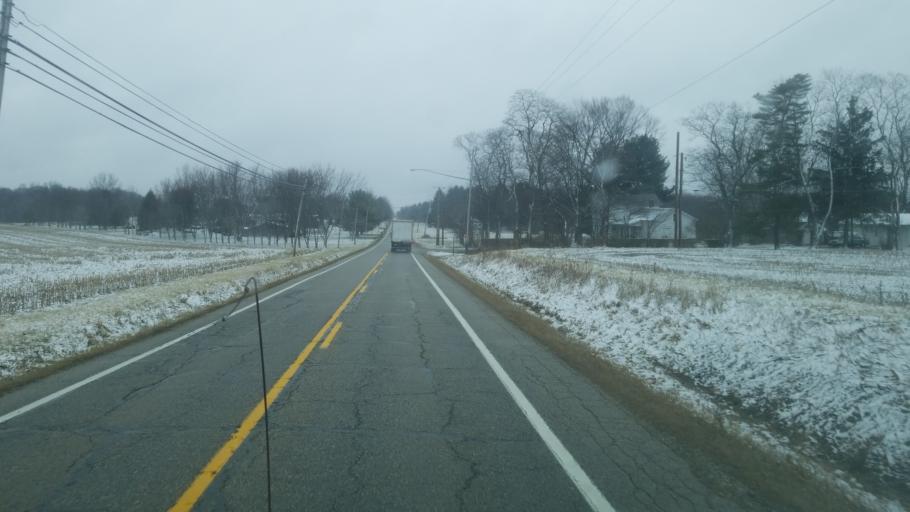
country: US
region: Ohio
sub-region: Portage County
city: Garrettsville
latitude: 41.2537
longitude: -81.1174
